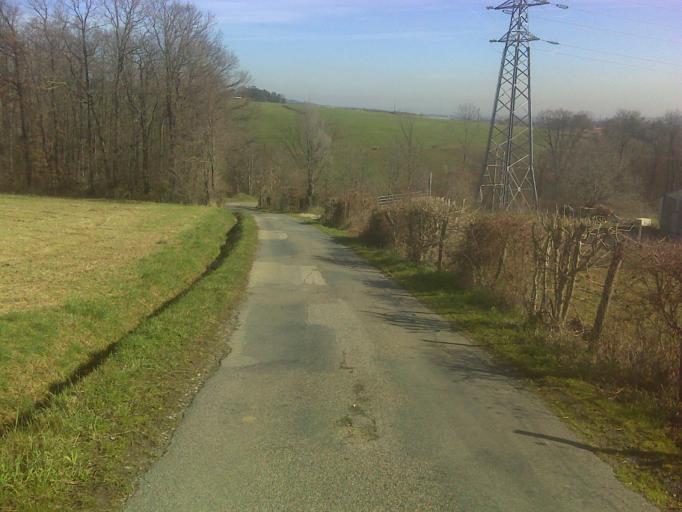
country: FR
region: Rhone-Alpes
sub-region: Departement du Rhone
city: Lentilly
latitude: 45.8231
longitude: 4.6490
